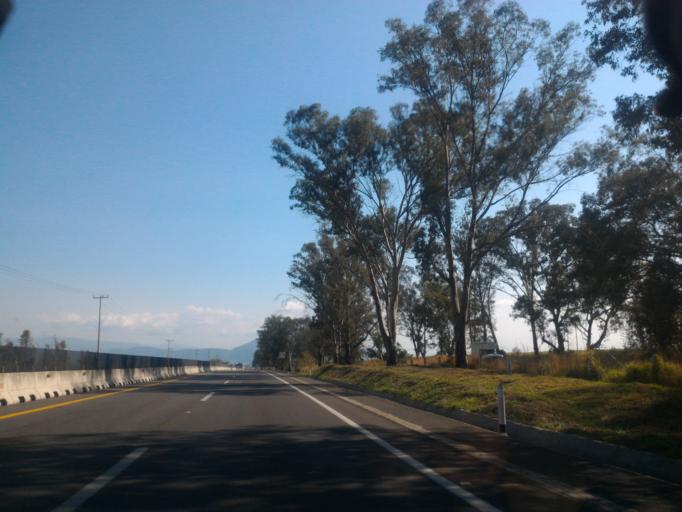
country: MX
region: Jalisco
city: Zapotiltic
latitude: 19.5880
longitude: -103.4505
